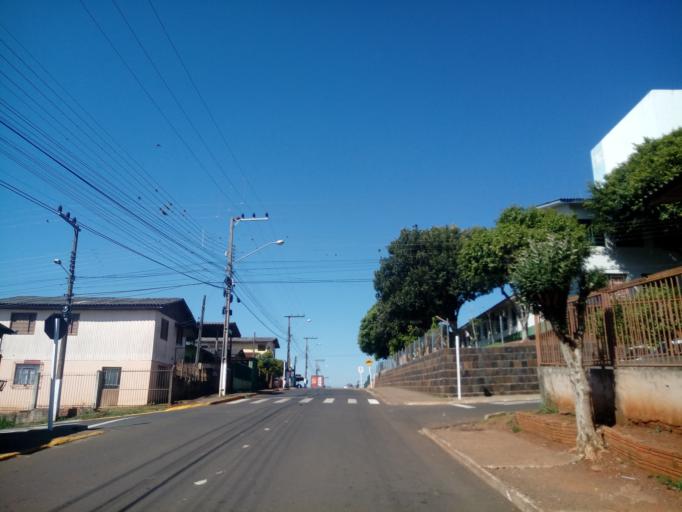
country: BR
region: Santa Catarina
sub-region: Chapeco
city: Chapeco
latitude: -27.0921
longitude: -52.6740
